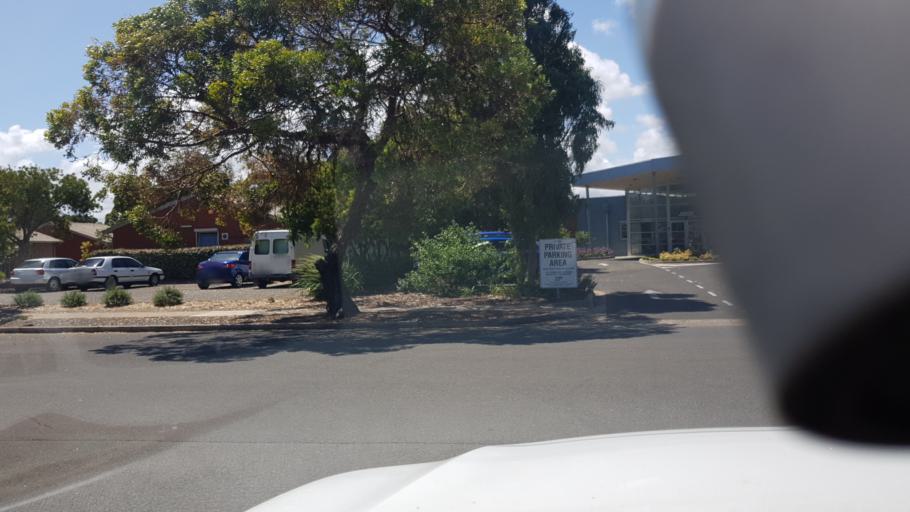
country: AU
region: South Australia
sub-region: Holdfast Bay
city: North Brighton
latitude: -35.0087
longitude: 138.5278
